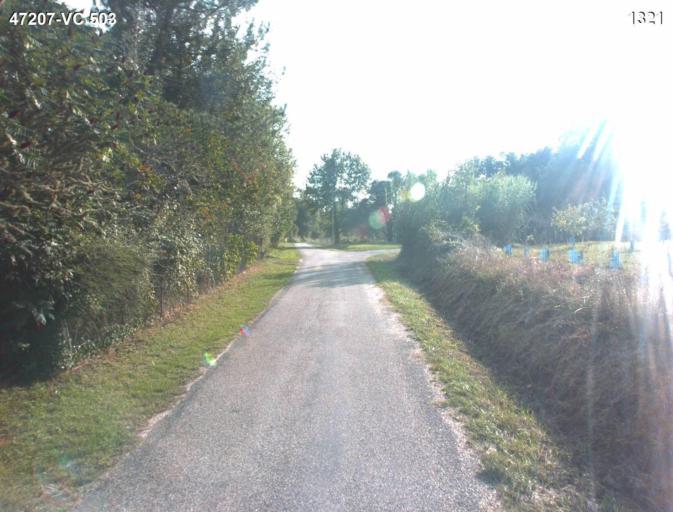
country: FR
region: Aquitaine
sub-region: Departement du Lot-et-Garonne
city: Barbaste
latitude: 44.1951
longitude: 0.2311
